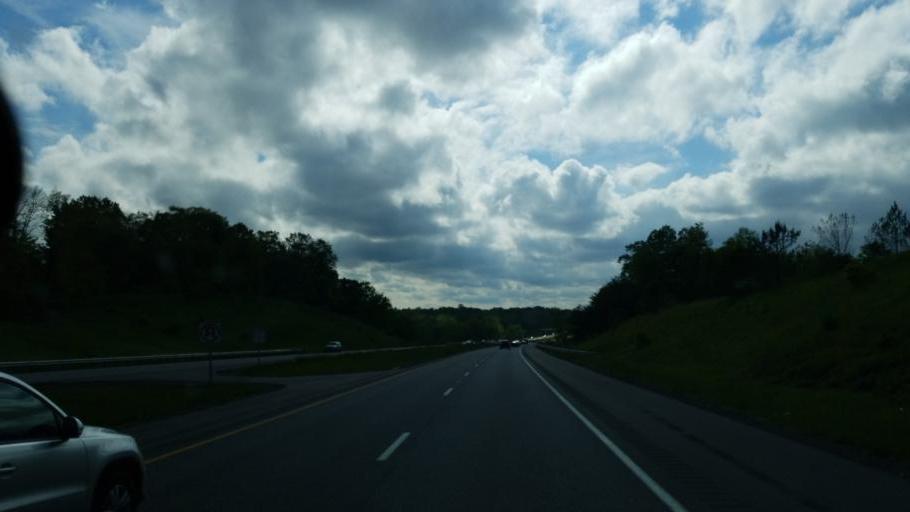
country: US
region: Ohio
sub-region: Geauga County
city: Bainbridge
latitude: 41.3882
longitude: -81.3762
